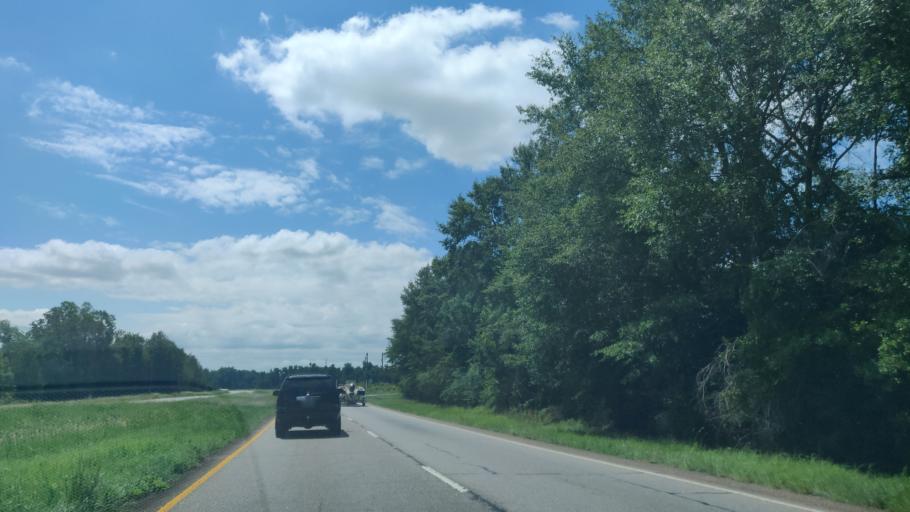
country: US
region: Georgia
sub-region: Stewart County
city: Richland
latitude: 32.0033
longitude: -84.6485
